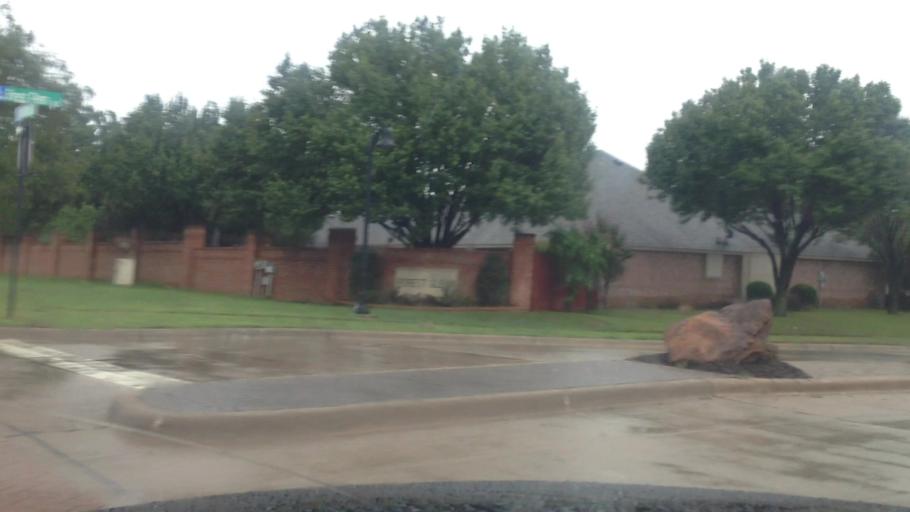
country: US
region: Texas
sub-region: Tarrant County
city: Keller
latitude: 32.9021
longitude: -97.2067
